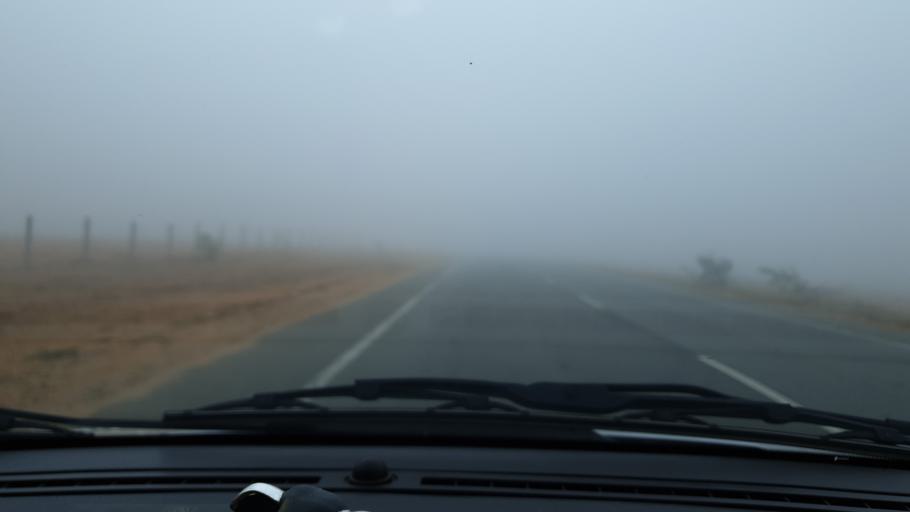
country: IN
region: Telangana
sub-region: Mahbubnagar
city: Nagar Karnul
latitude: 16.6821
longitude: 78.5257
